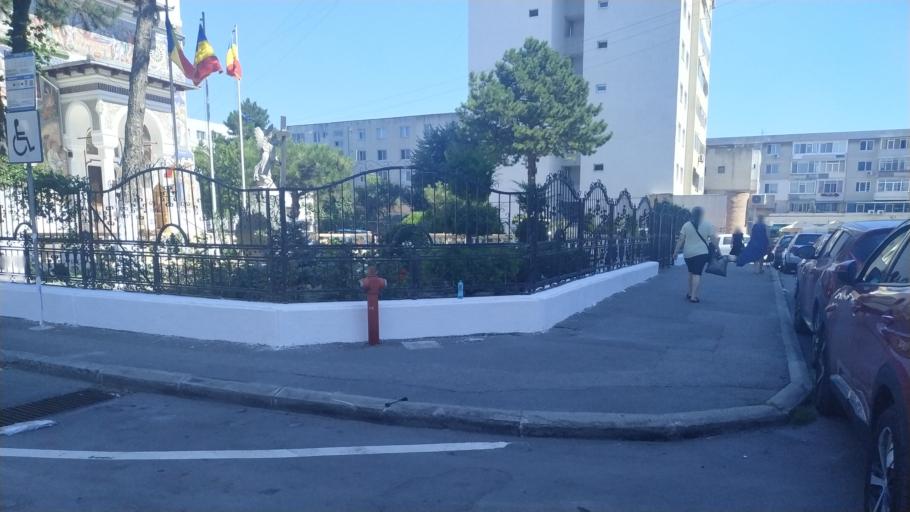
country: RO
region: Constanta
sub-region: Municipiul Constanta
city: Constanta
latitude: 44.1792
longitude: 28.6468
